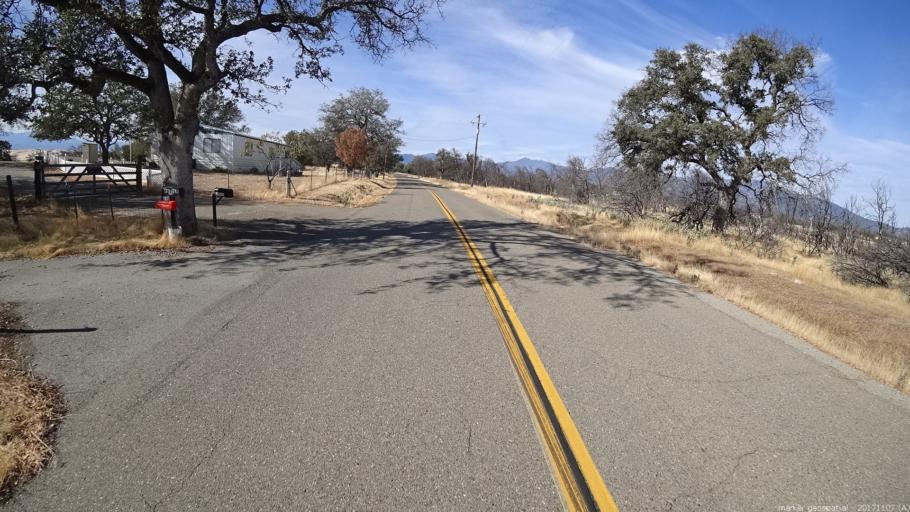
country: US
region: California
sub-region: Shasta County
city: Shasta
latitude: 40.4557
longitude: -122.5337
